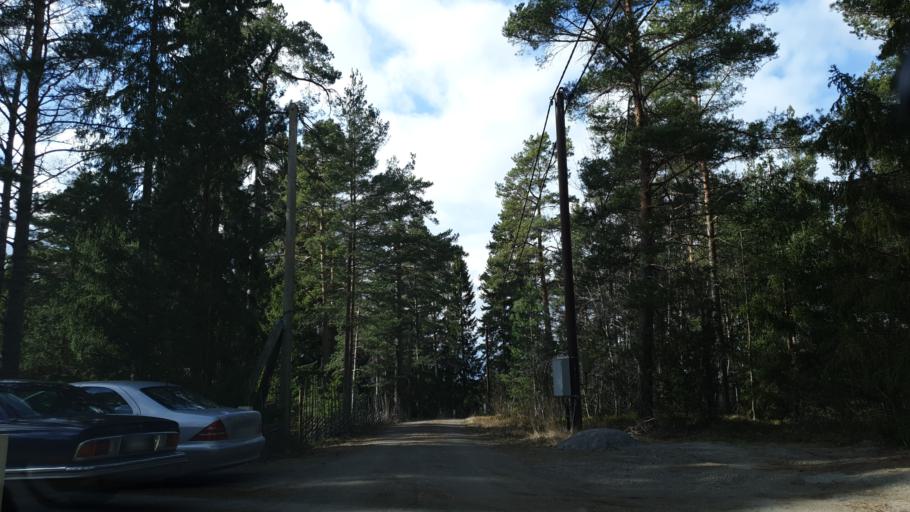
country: SE
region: Stockholm
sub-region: Varmdo Kommun
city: Mortnas
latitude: 59.2643
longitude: 18.4234
